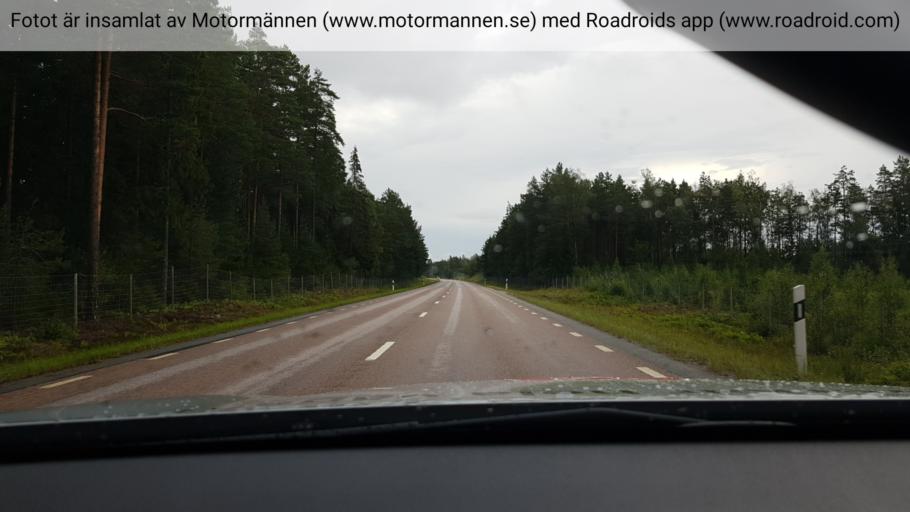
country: SE
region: Uppsala
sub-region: Tierps Kommun
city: Karlholmsbruk
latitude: 60.4306
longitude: 17.8146
